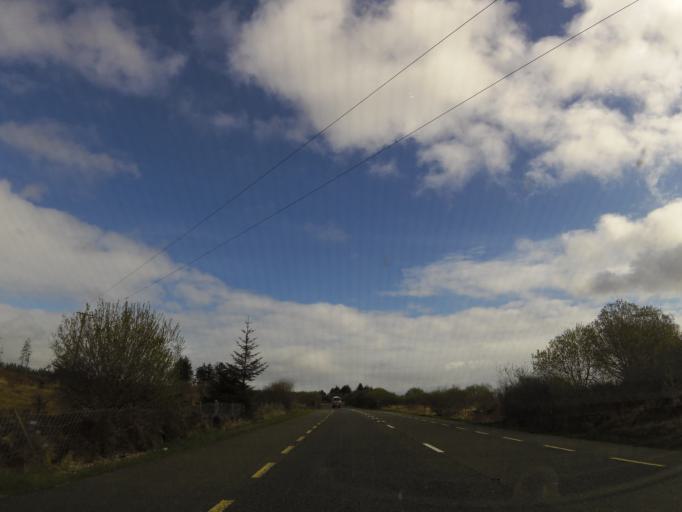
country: IE
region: Connaught
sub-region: Maigh Eo
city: Ballyhaunis
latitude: 53.9046
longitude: -8.7957
